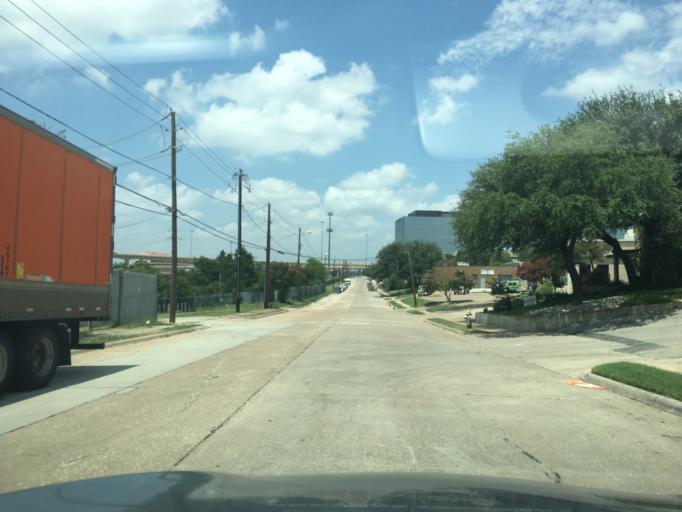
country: US
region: Texas
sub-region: Dallas County
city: Richardson
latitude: 32.9190
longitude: -96.7611
